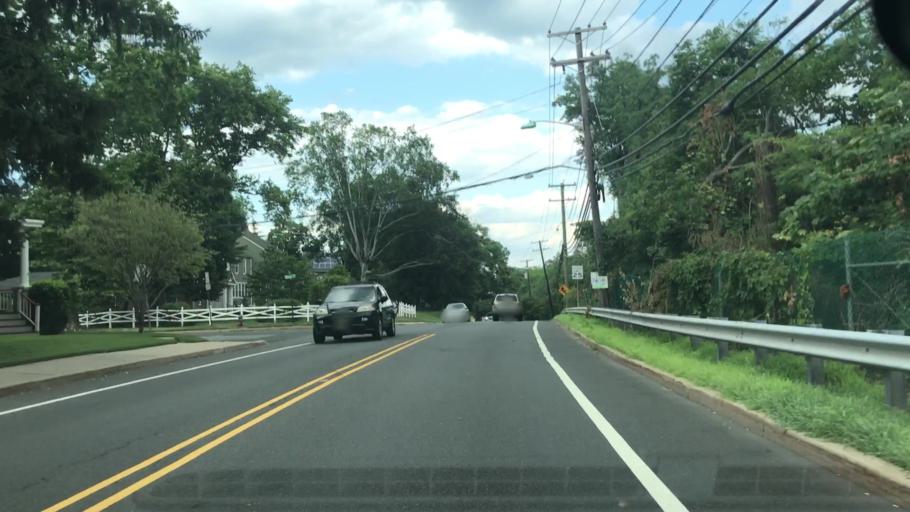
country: US
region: New Jersey
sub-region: Somerset County
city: Raritan
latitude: 40.5639
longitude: -74.6416
